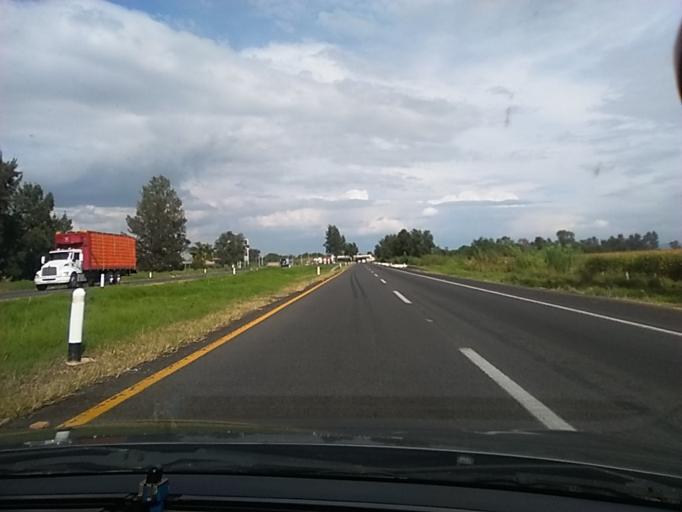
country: MX
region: Jalisco
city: La Barca
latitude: 20.3219
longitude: -102.5146
